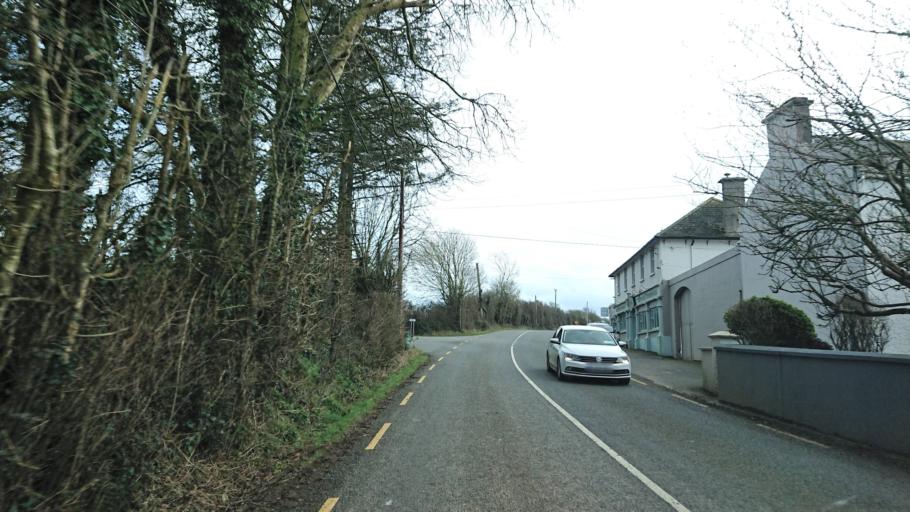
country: IE
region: Munster
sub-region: Waterford
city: Dunmore East
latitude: 52.2456
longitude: -6.9025
